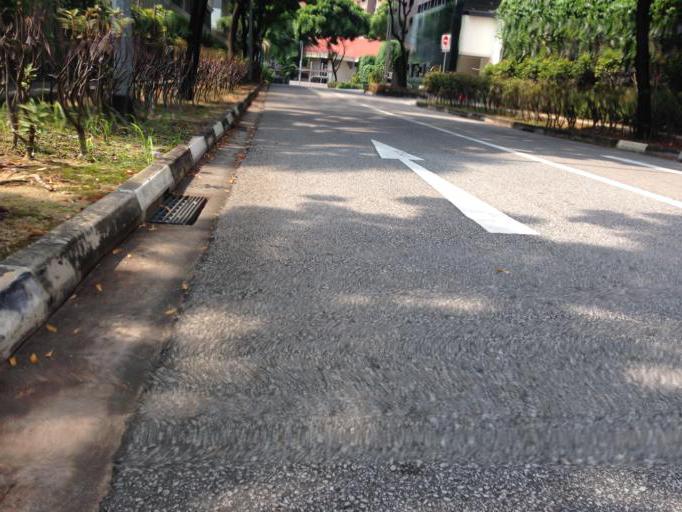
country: SG
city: Singapore
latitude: 1.3021
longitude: 103.8516
